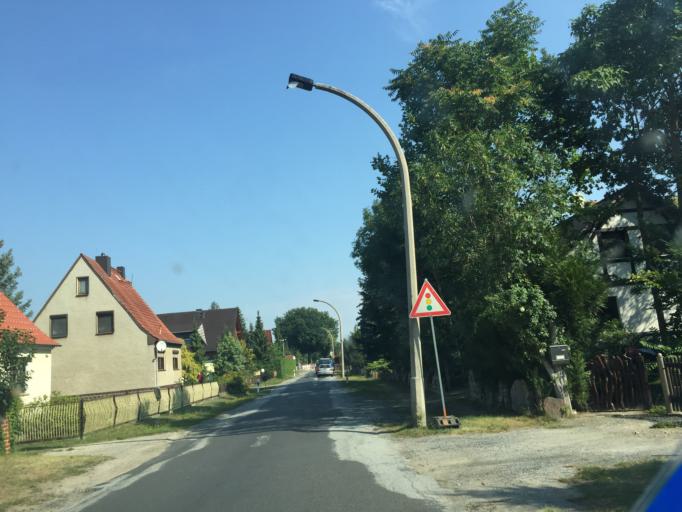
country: DE
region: Saxony
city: Uhyst
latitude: 51.3593
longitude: 14.5080
